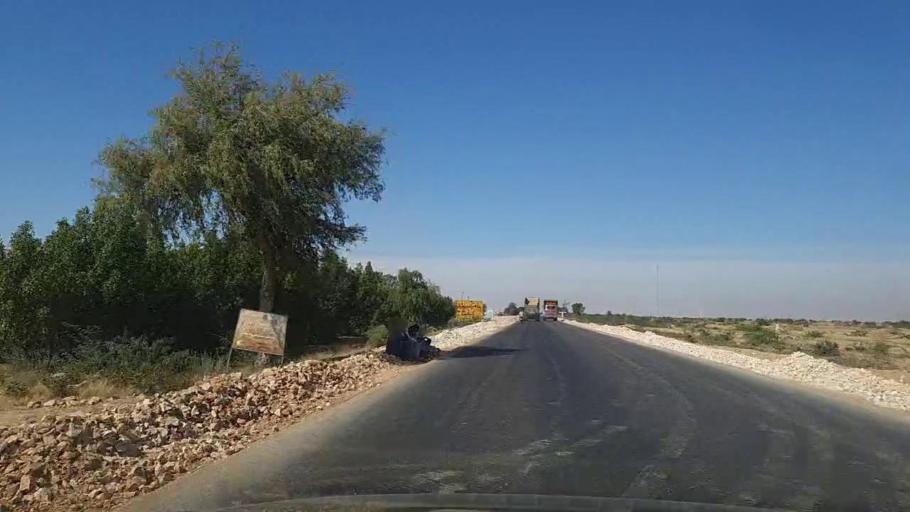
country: PK
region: Sindh
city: Kotri
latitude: 25.2629
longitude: 68.2213
